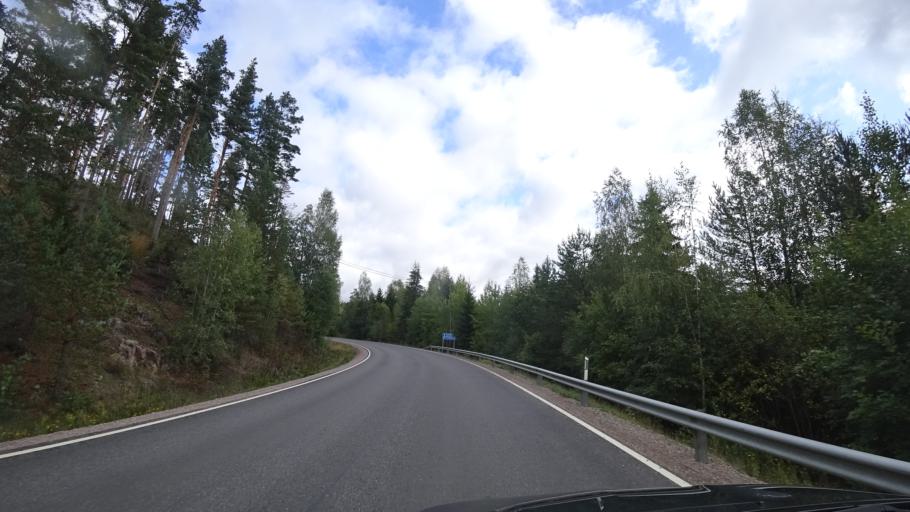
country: FI
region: Haeme
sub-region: Haemeenlinna
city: Lammi
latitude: 60.9440
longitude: 25.0163
